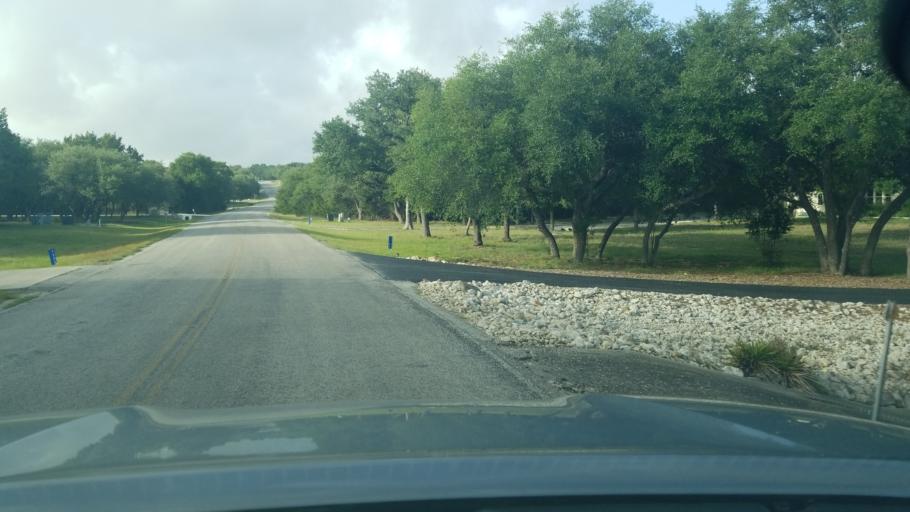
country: US
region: Texas
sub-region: Comal County
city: Bulverde
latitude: 29.8335
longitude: -98.4072
